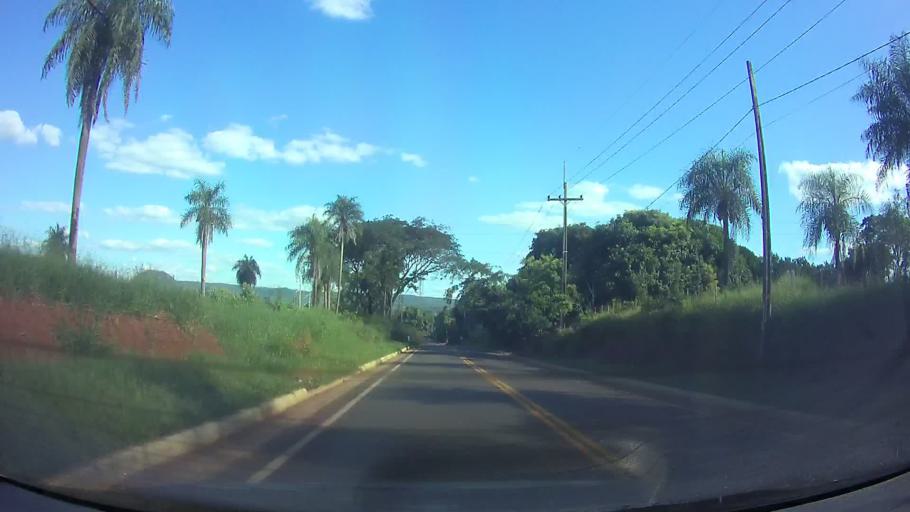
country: PY
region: Cordillera
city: Caacupe
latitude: -25.3690
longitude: -57.1422
